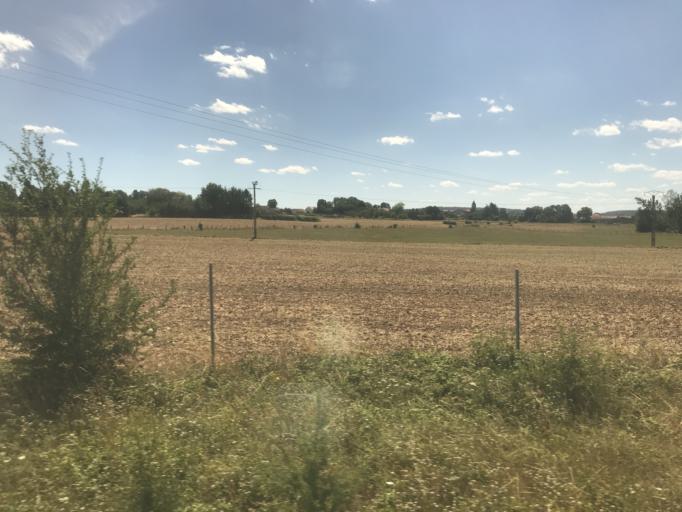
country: FR
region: Lorraine
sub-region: Departement de la Moselle
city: Remilly
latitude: 48.9683
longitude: 6.4566
